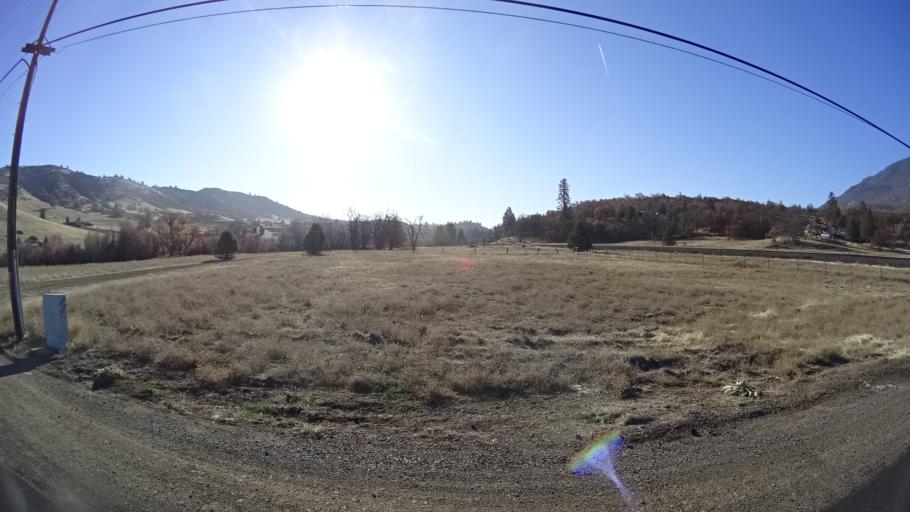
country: US
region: California
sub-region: Siskiyou County
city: Montague
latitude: 41.8896
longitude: -122.4830
